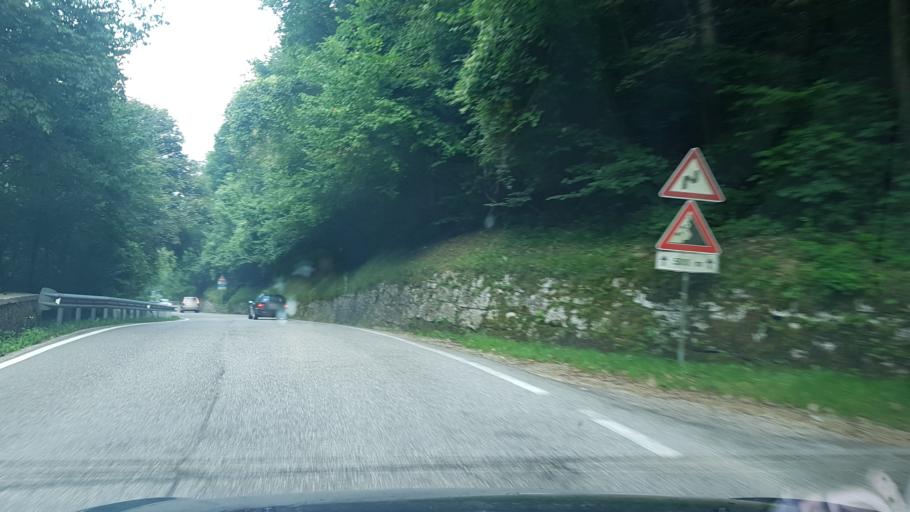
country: IT
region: Veneto
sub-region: Provincia di Vicenza
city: Recoaro Terme
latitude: 45.7590
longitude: 11.2085
